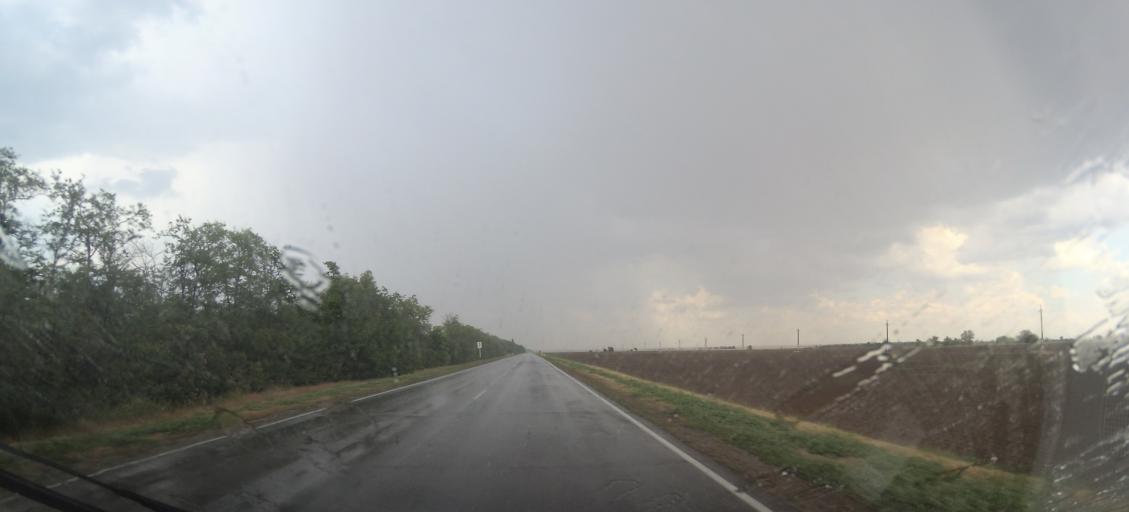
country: RU
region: Rostov
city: Proletarsk
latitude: 46.6547
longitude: 41.6807
